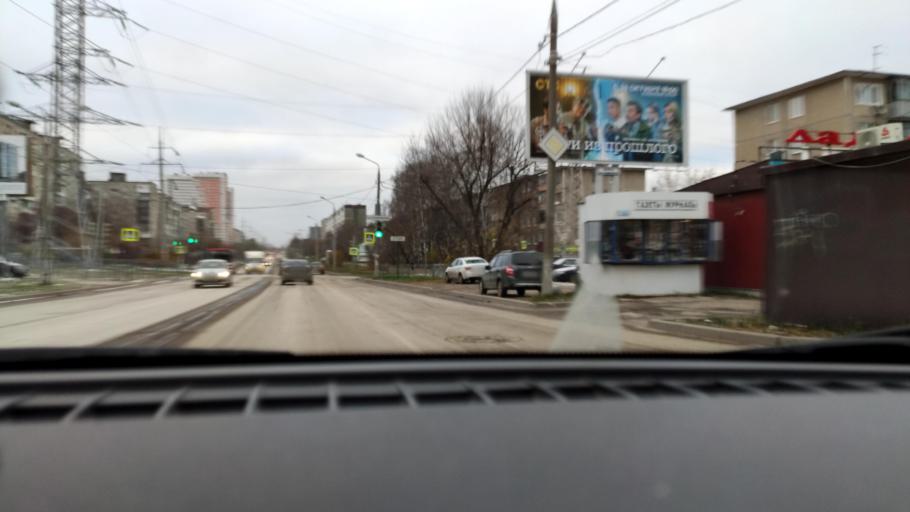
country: RU
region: Perm
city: Perm
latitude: 57.9803
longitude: 56.2140
